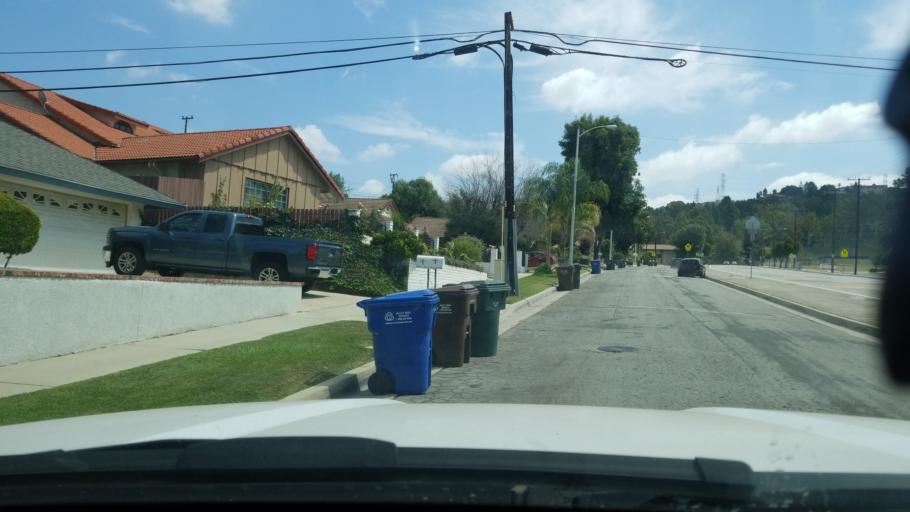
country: US
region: California
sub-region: Los Angeles County
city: Hacienda Heights
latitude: 33.9858
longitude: -117.9620
